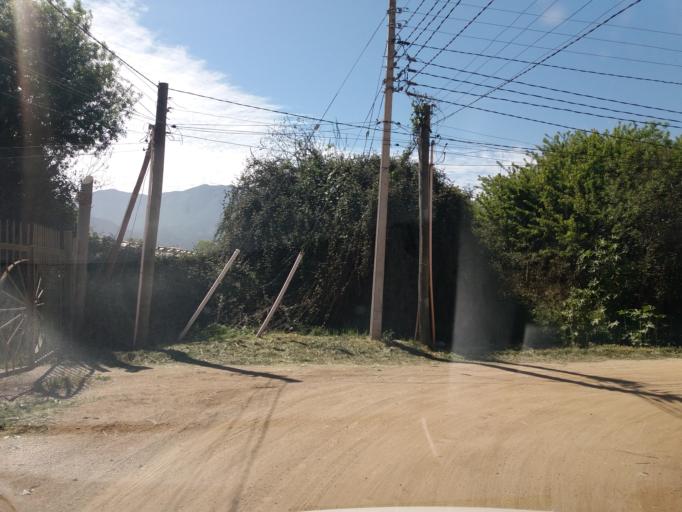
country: CL
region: Valparaiso
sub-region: Provincia de Quillota
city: Quillota
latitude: -32.8714
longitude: -71.2187
